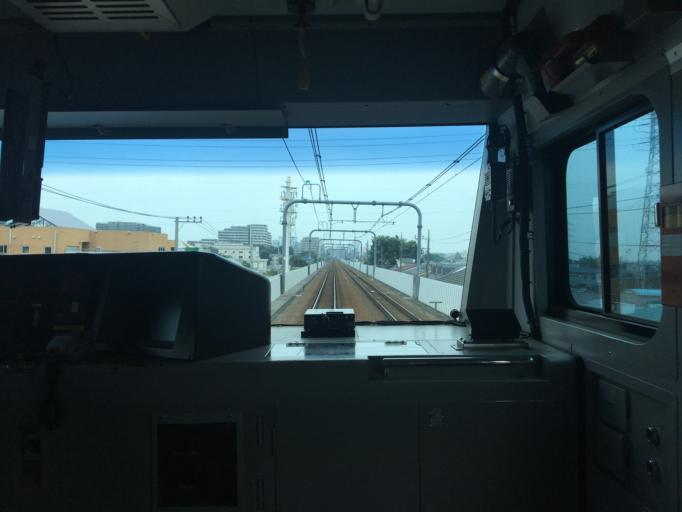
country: JP
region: Tokyo
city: Nishi-Tokyo-shi
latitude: 35.7017
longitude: 139.5281
